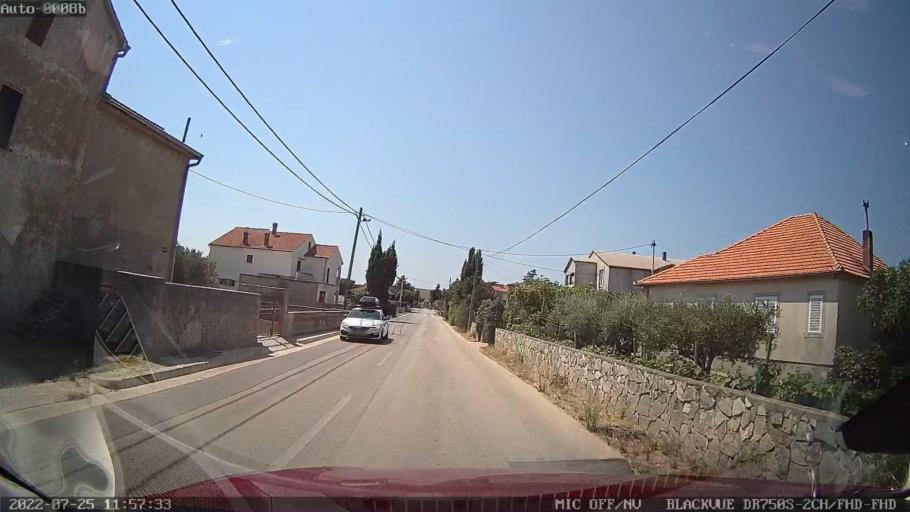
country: HR
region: Zadarska
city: Vrsi
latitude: 44.2423
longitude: 15.2138
